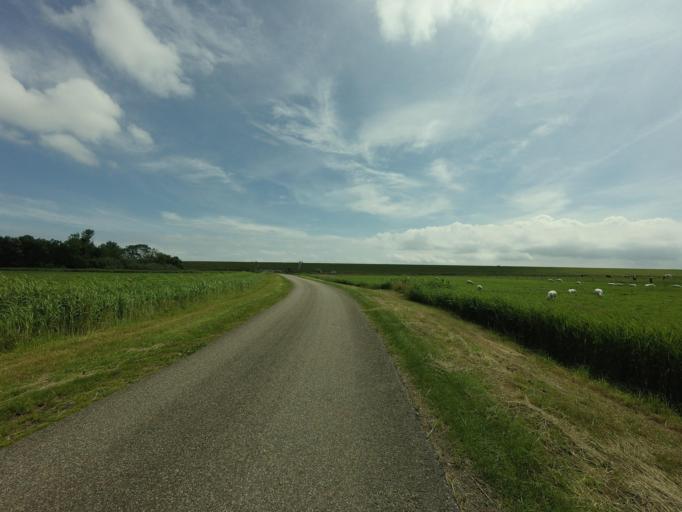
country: NL
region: North Holland
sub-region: Gemeente Texel
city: Den Burg
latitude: 53.0649
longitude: 4.8689
